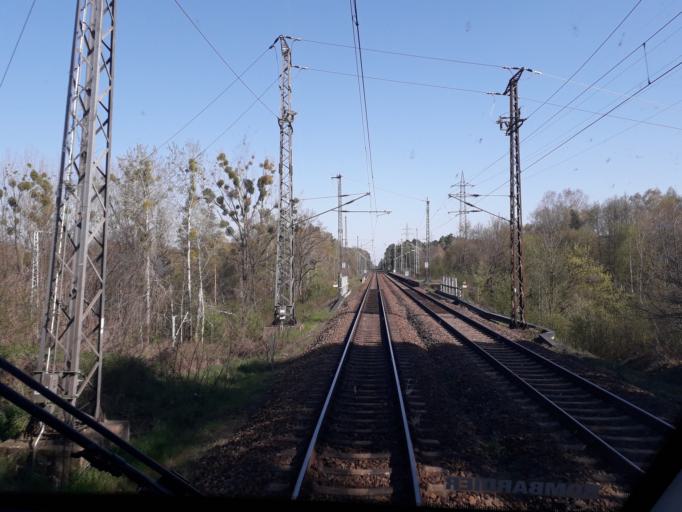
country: DE
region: Brandenburg
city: Michendorf
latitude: 52.3405
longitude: 13.0797
